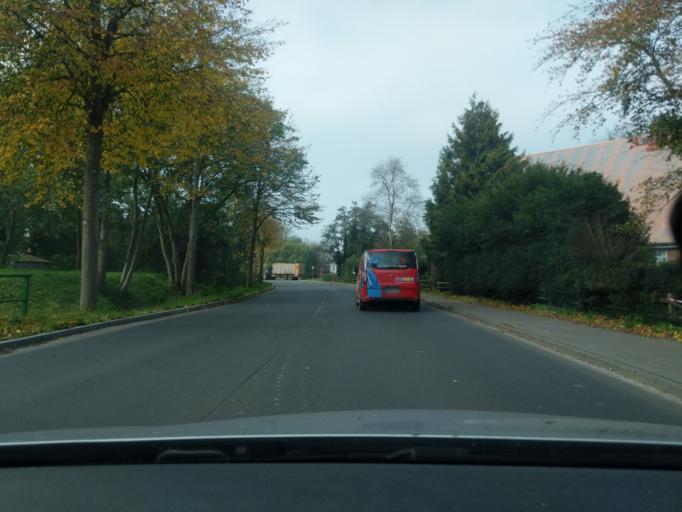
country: DE
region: Lower Saxony
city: Belum
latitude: 53.8173
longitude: 8.9931
